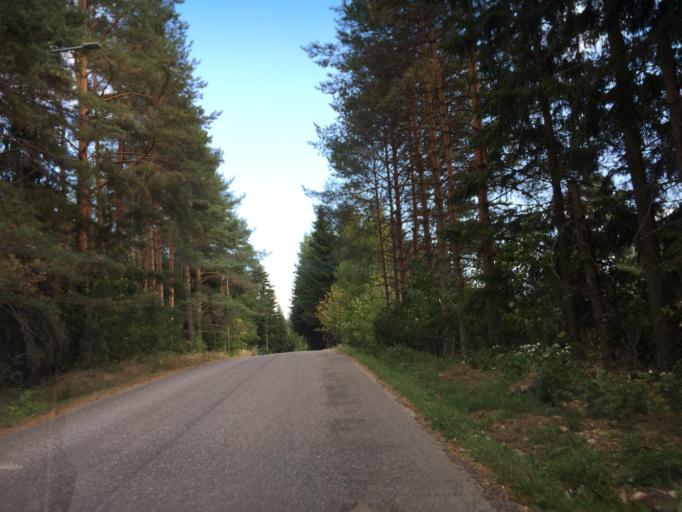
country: FI
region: Haeme
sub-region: Haemeenlinna
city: Tuulos
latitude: 61.0723
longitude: 24.6743
